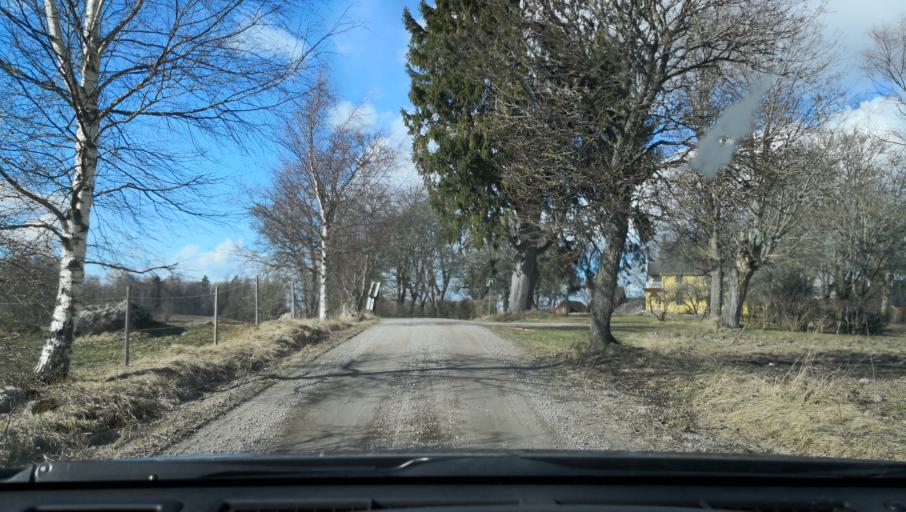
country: SE
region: OErebro
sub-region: Lindesbergs Kommun
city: Fellingsbro
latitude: 59.4175
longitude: 15.6331
